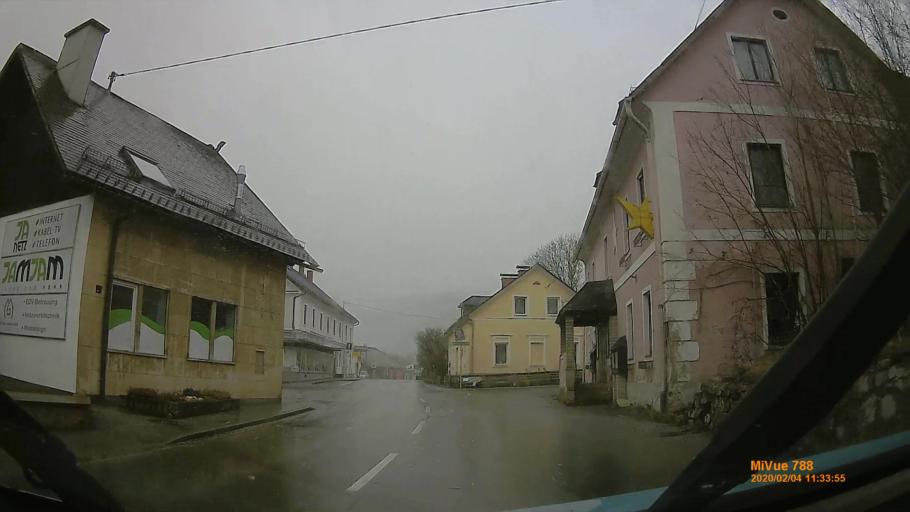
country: AT
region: Styria
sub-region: Politischer Bezirk Bruck-Muerzzuschlag
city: Neuberg an der Muerz
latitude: 47.6667
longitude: 15.5753
